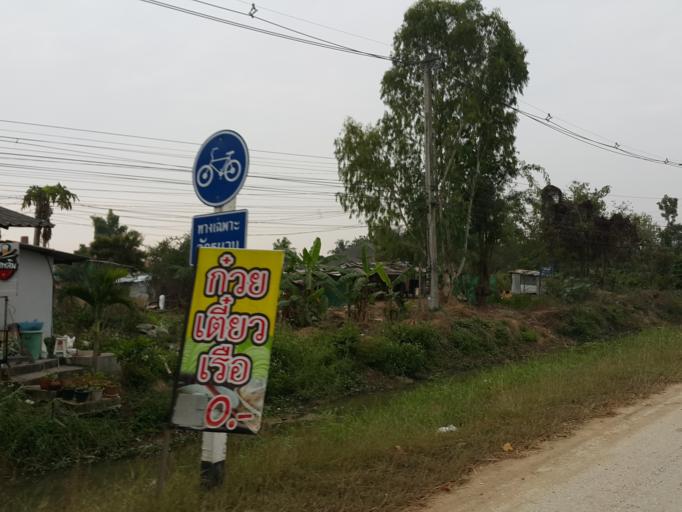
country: TH
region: Chiang Mai
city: San Kamphaeng
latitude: 18.7533
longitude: 99.0729
